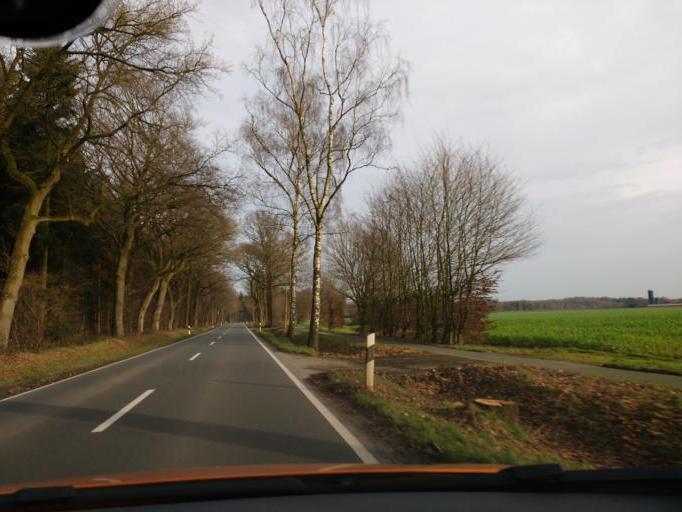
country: DE
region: Lower Saxony
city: Hude
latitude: 53.0538
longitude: 8.4540
